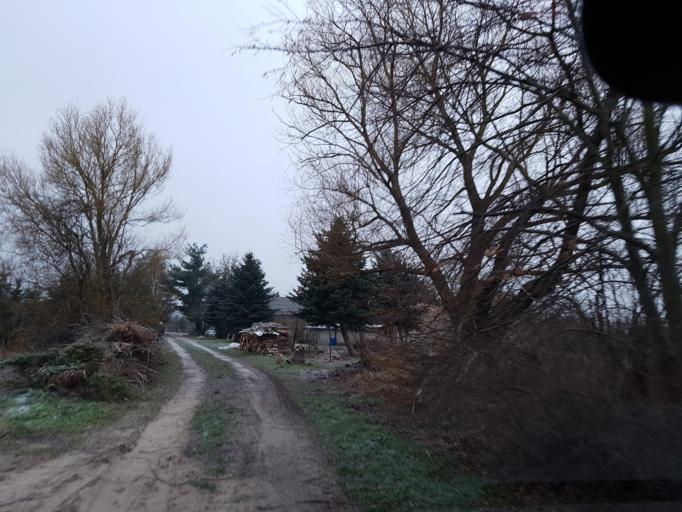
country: DE
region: Brandenburg
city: Ruckersdorf
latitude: 51.5666
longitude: 13.5467
